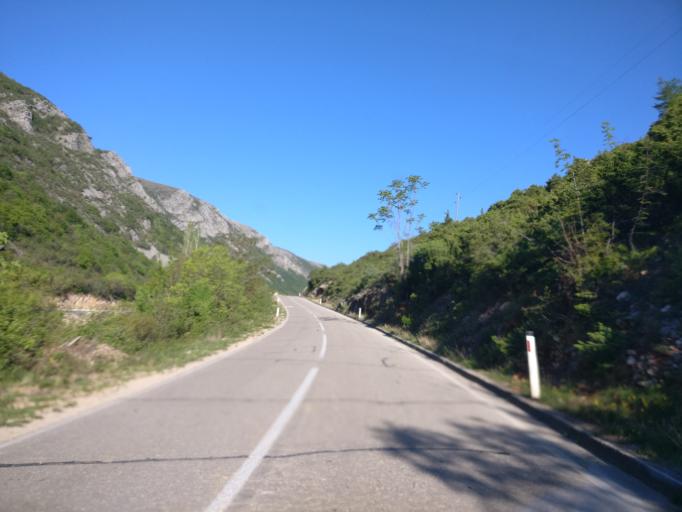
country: BA
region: Federation of Bosnia and Herzegovina
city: Stolac
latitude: 43.0756
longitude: 18.0273
